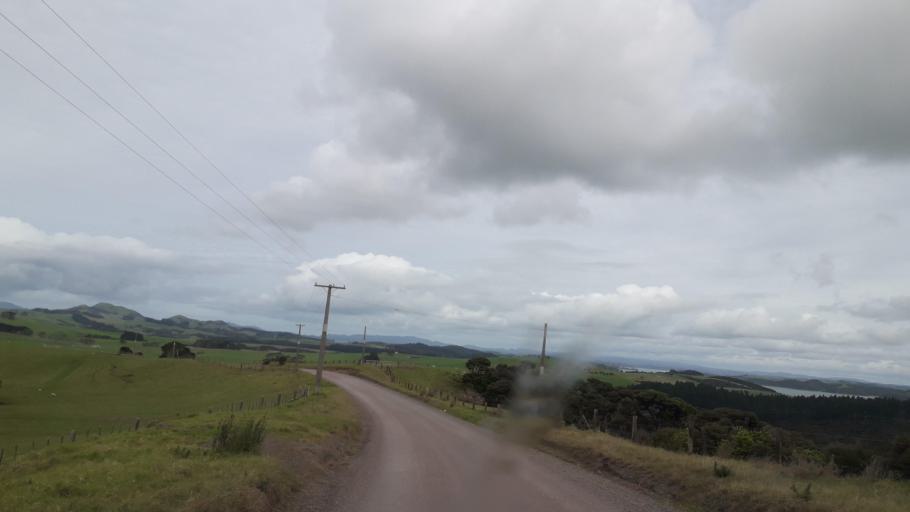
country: NZ
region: Northland
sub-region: Far North District
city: Kerikeri
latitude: -35.1346
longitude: 174.0174
